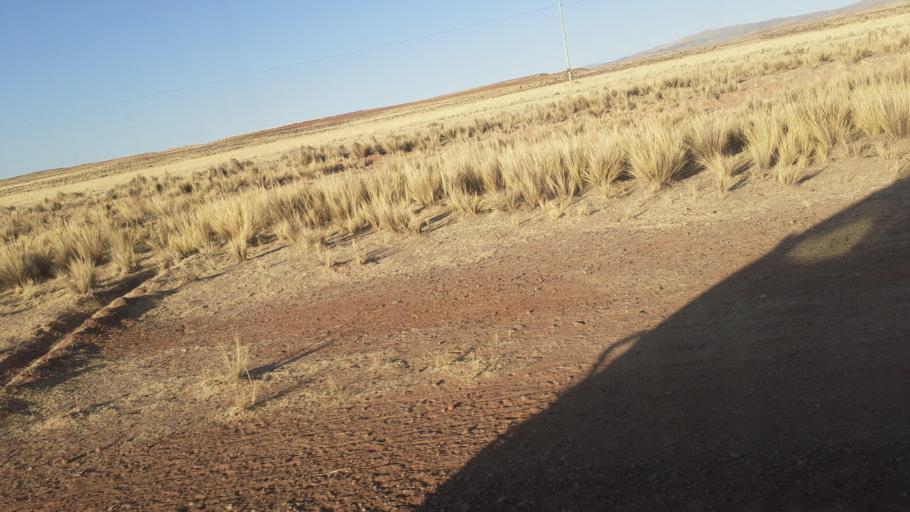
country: BO
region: La Paz
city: Tiahuanaco
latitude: -16.9538
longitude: -68.7587
